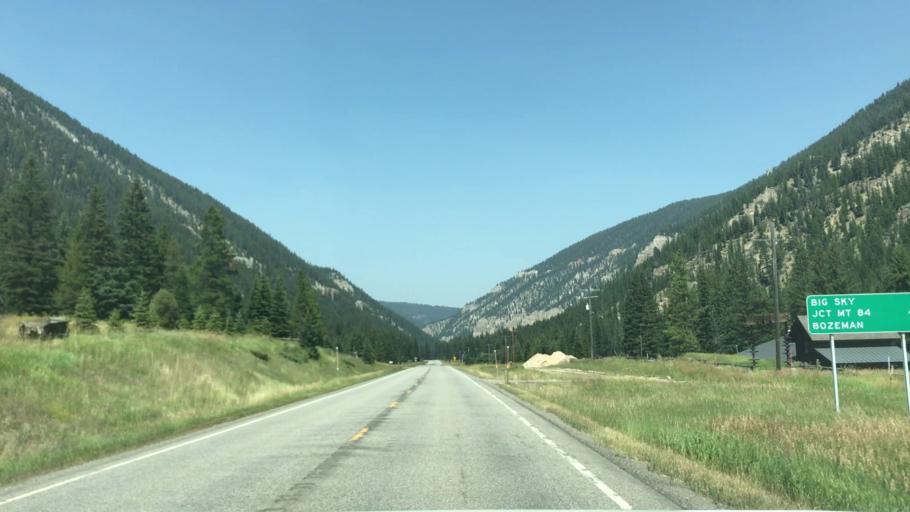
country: US
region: Montana
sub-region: Gallatin County
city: Big Sky
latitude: 45.1187
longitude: -111.2269
